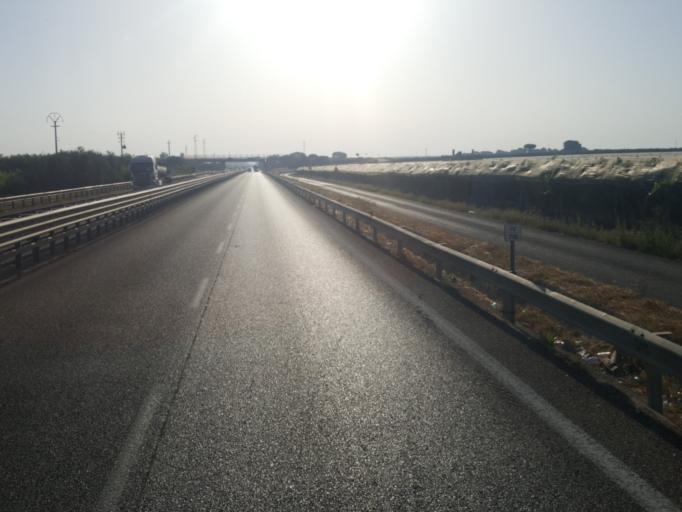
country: IT
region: Apulia
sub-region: Provincia di Foggia
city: Cerignola
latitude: 41.2685
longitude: 15.9480
